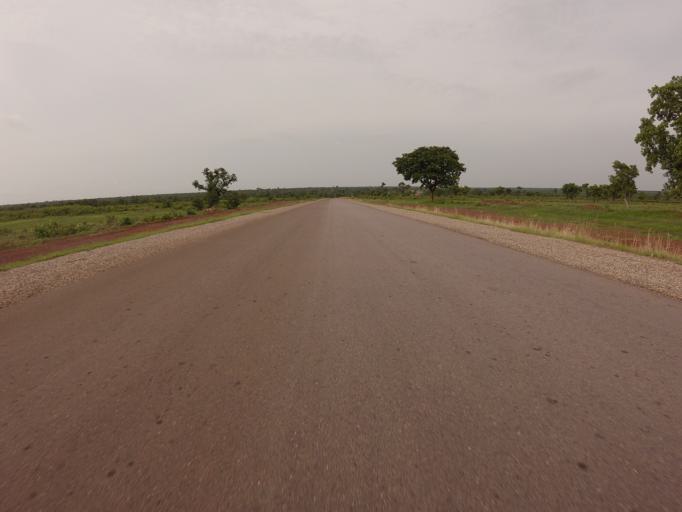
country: GH
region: Northern
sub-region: Yendi
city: Yendi
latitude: 9.8007
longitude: -0.1133
